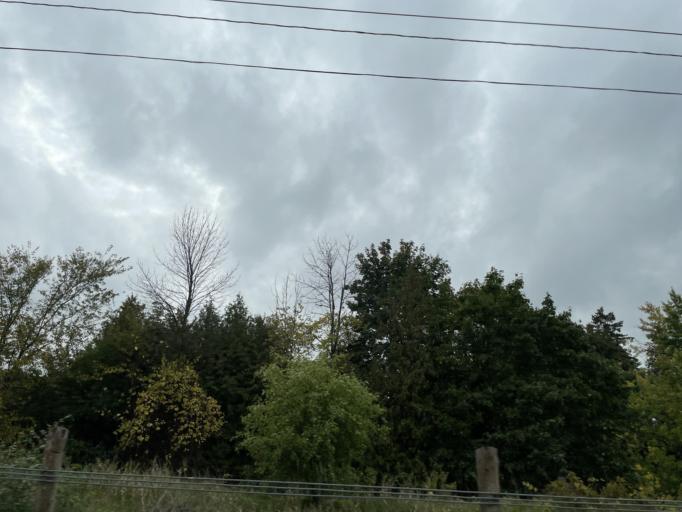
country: CA
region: Ontario
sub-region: Wellington County
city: Guelph
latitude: 43.5597
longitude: -80.2055
